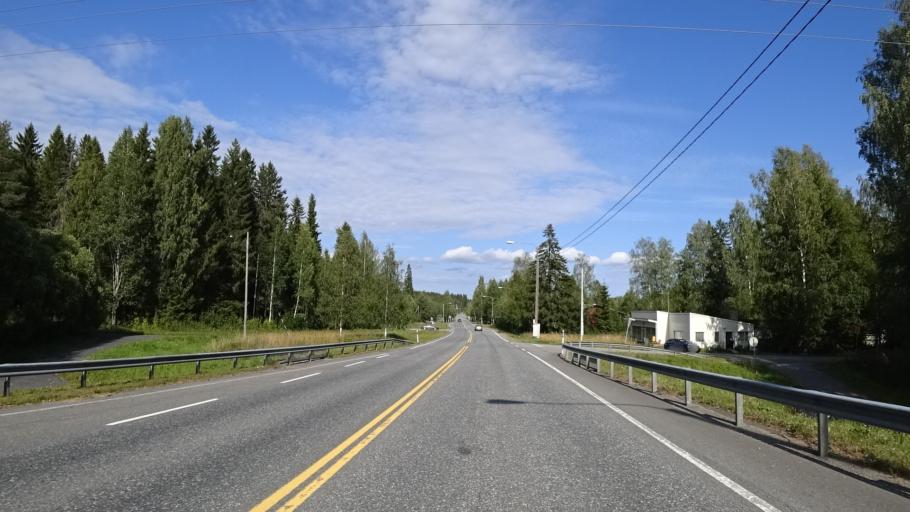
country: FI
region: North Karelia
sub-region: Joensuu
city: Eno
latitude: 62.8000
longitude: 30.1129
